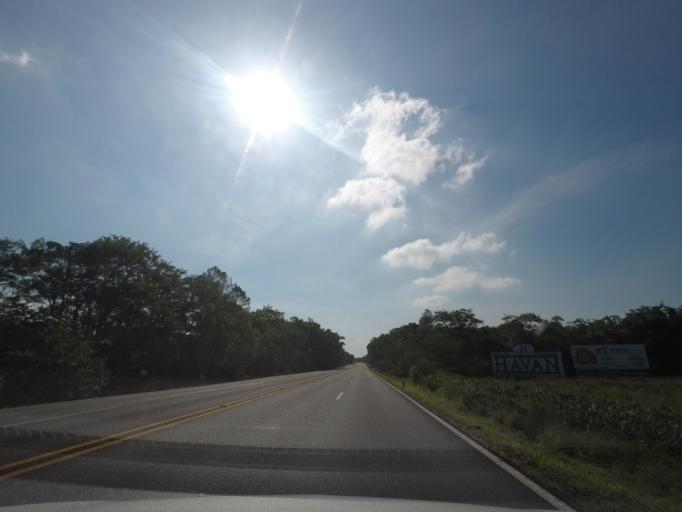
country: BR
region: Parana
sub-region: Pontal Do Parana
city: Pontal do Parana
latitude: -25.6358
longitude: -48.5931
